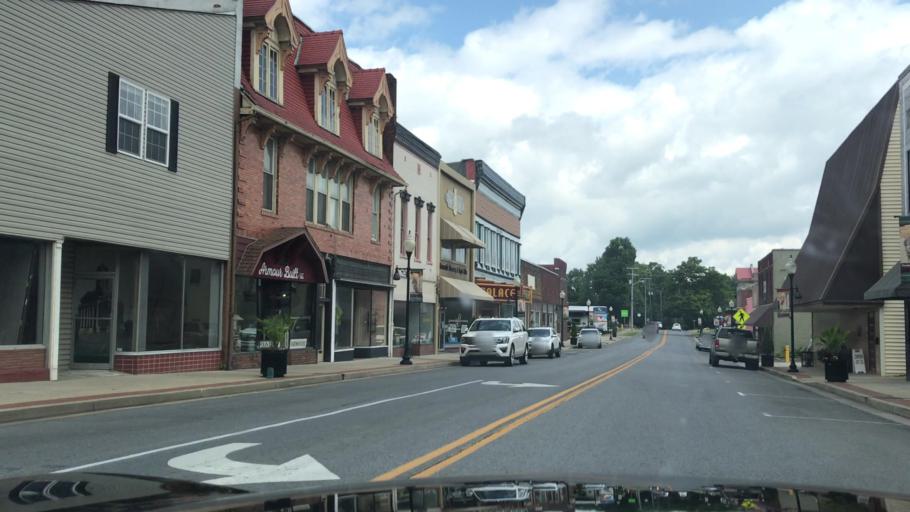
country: US
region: Kentucky
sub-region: Muhlenberg County
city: Greenville
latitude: 37.2012
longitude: -87.1785
